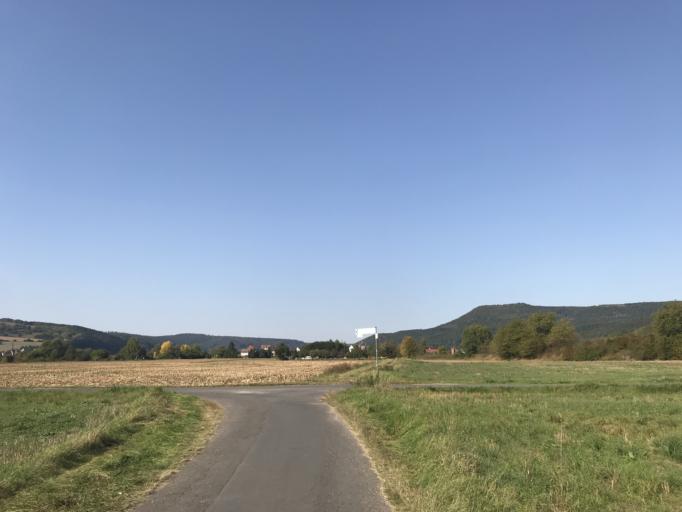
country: DE
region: Thuringia
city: Treffurt
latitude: 51.1311
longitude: 10.1881
